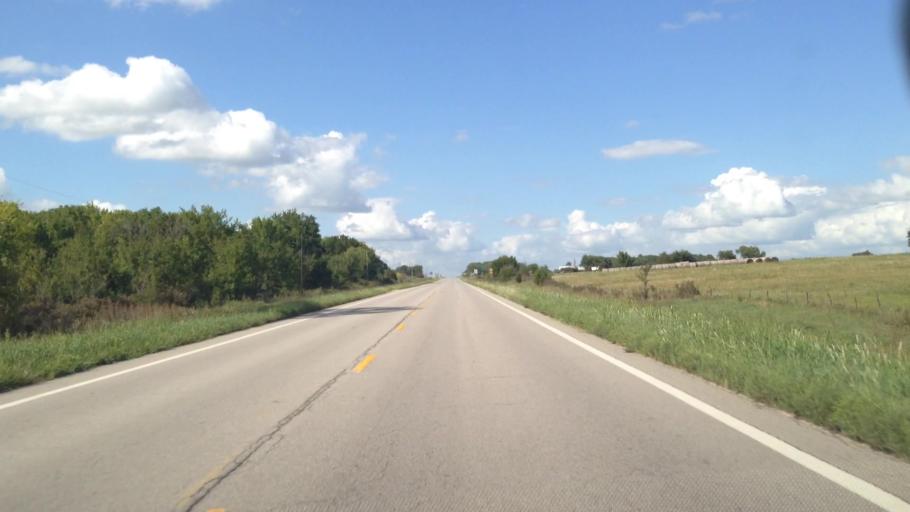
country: US
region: Kansas
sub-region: Neosho County
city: Erie
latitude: 37.7145
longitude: -95.1607
